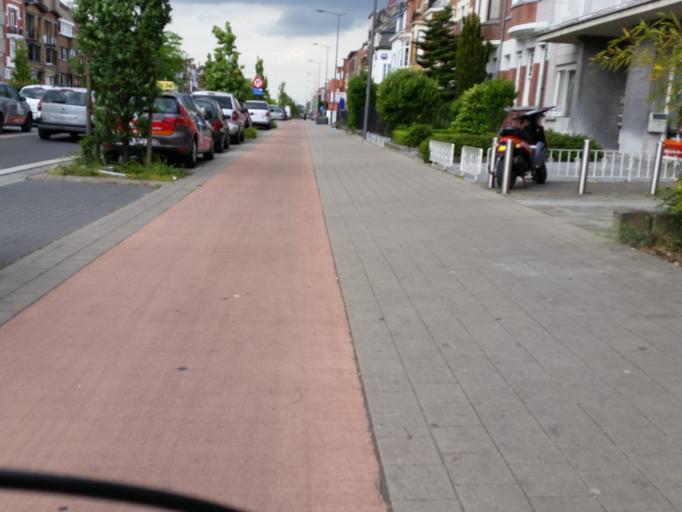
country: BE
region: Flanders
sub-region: Provincie Vlaams-Brabant
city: Vilvoorde
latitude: 50.9310
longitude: 4.4287
